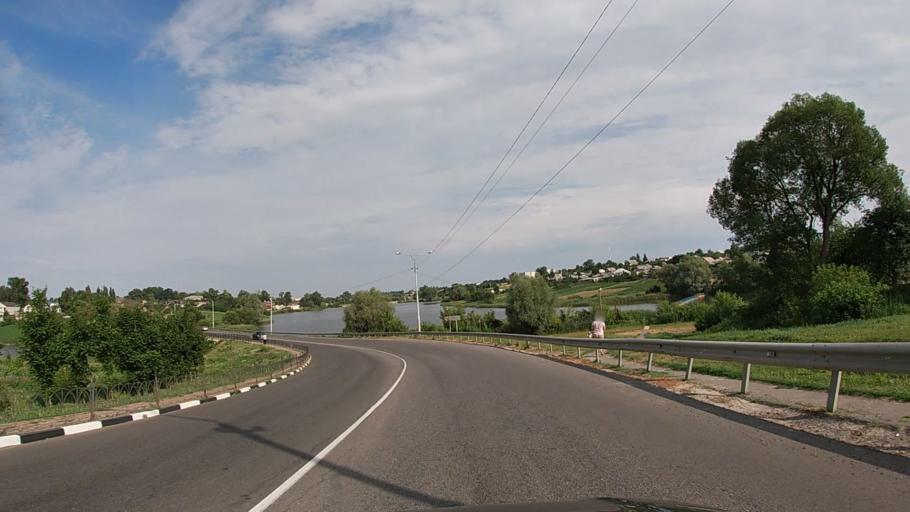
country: RU
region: Belgorod
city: Krasnaya Yaruga
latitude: 50.8008
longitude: 35.6716
